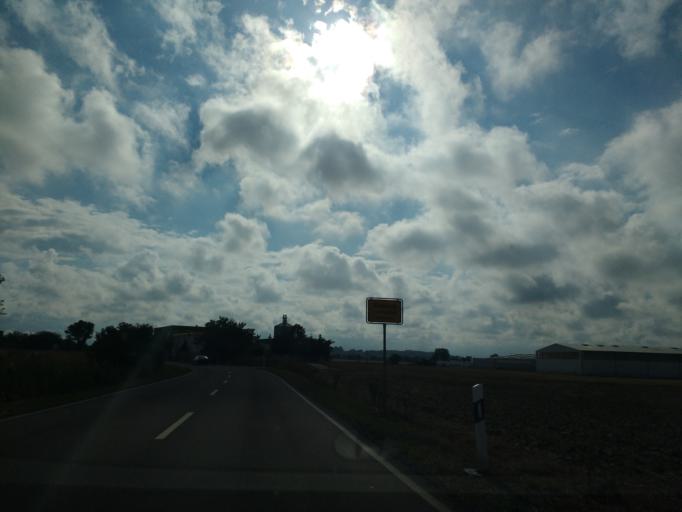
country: DE
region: Saxony-Anhalt
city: Niemberg
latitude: 51.5556
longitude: 12.1095
